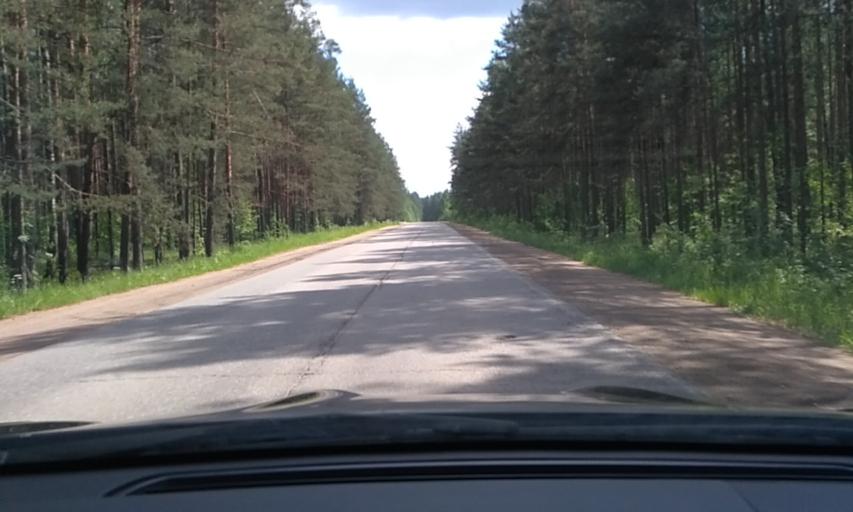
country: RU
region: Leningrad
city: Imeni Sverdlova
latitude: 59.8467
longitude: 30.6850
